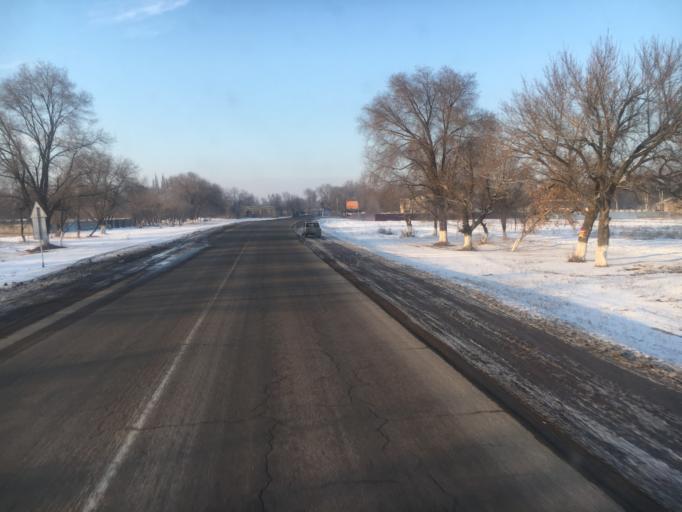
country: KZ
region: Almaty Oblysy
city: Burunday
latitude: 43.3640
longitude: 76.6422
